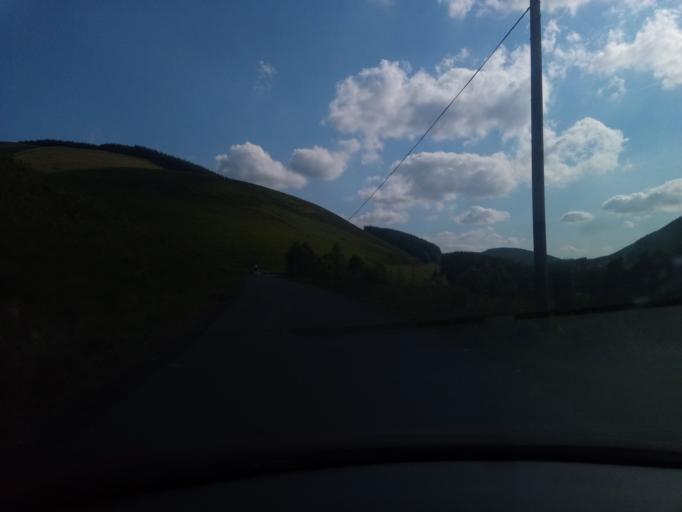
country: GB
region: Scotland
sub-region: The Scottish Borders
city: Innerleithen
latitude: 55.4820
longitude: -3.1337
